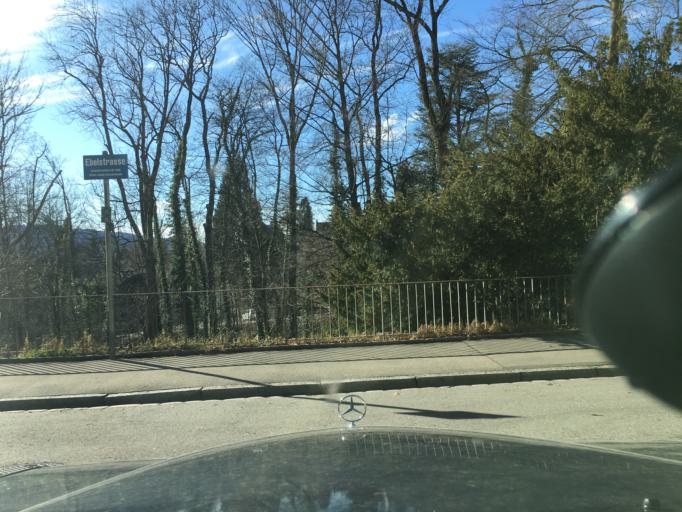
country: CH
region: Zurich
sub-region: Bezirk Zuerich
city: Zuerich (Kreis 7) / Hottingen
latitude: 47.3749
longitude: 8.5668
